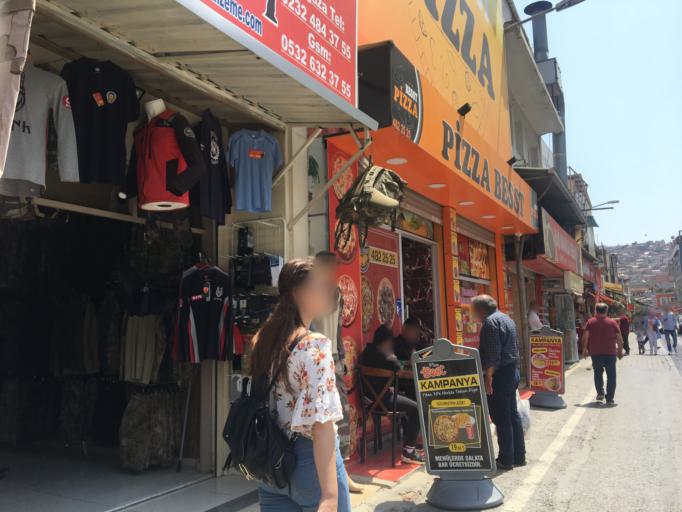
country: TR
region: Izmir
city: Izmir
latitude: 38.4202
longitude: 27.1311
